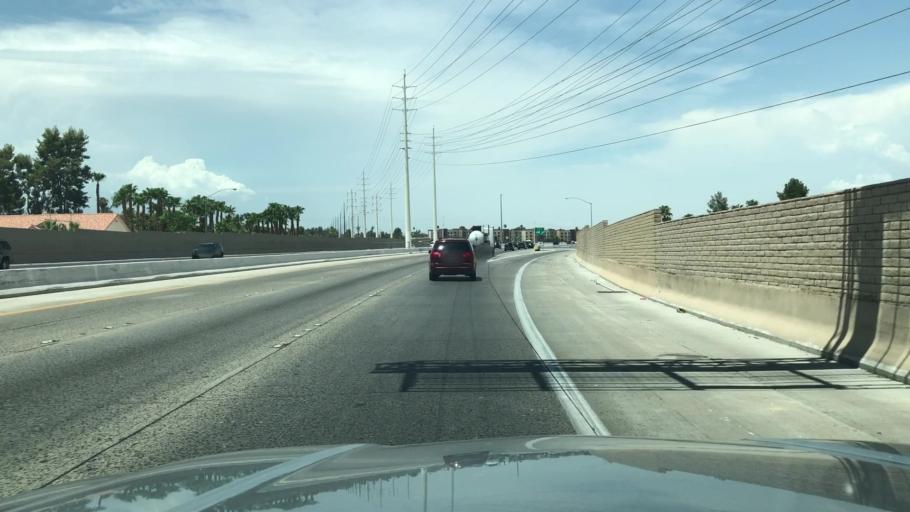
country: US
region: Nevada
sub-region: Clark County
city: Whitney
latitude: 36.0954
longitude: -115.0781
